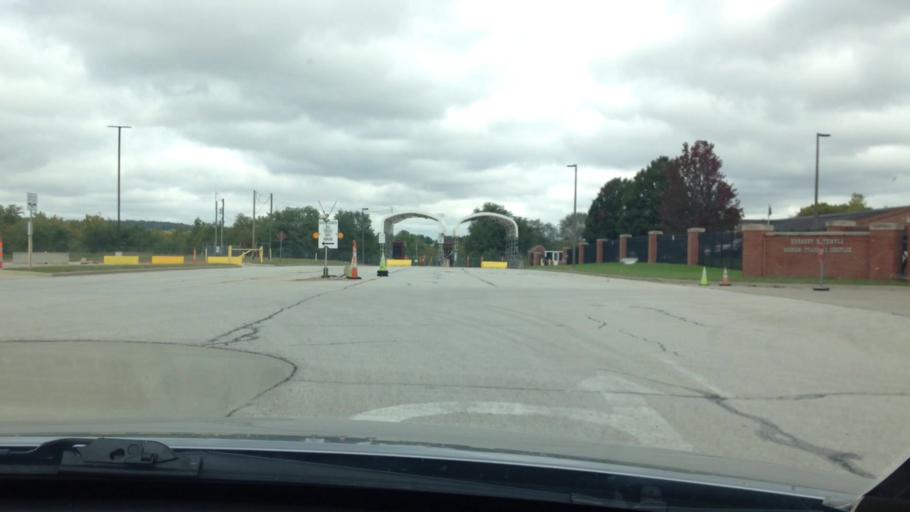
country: US
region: Kansas
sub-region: Leavenworth County
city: Leavenworth
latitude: 39.3299
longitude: -94.9162
